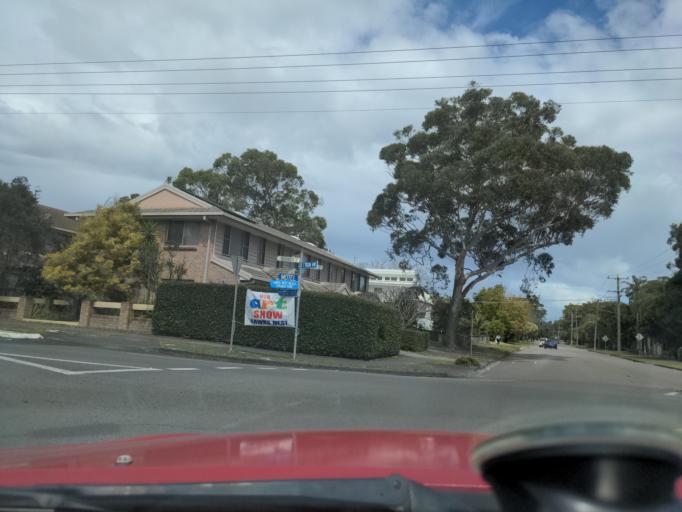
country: AU
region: New South Wales
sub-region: Great Lakes
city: Hawks Nest
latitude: -32.6726
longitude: 152.1774
